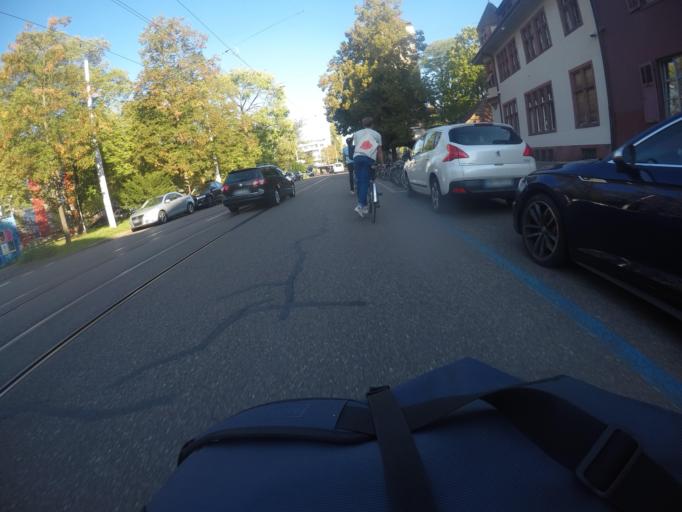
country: CH
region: Basel-City
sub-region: Basel-Stadt
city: Basel
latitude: 47.5660
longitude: 7.5824
